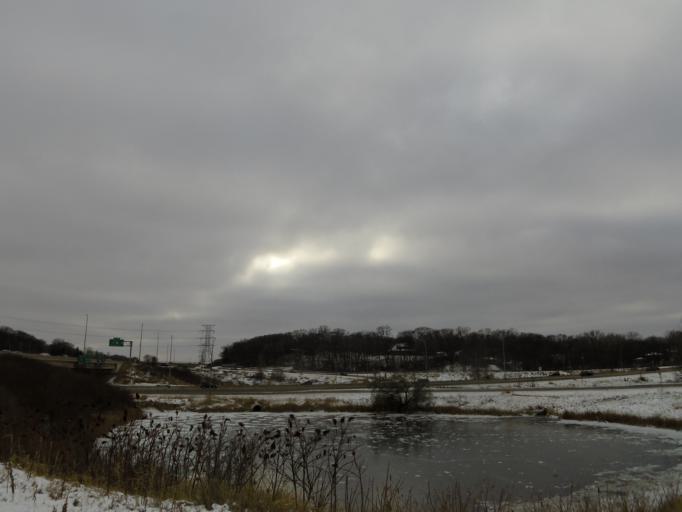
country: US
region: Minnesota
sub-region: Hennepin County
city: Minnetonka Mills
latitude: 44.9725
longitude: -93.4613
